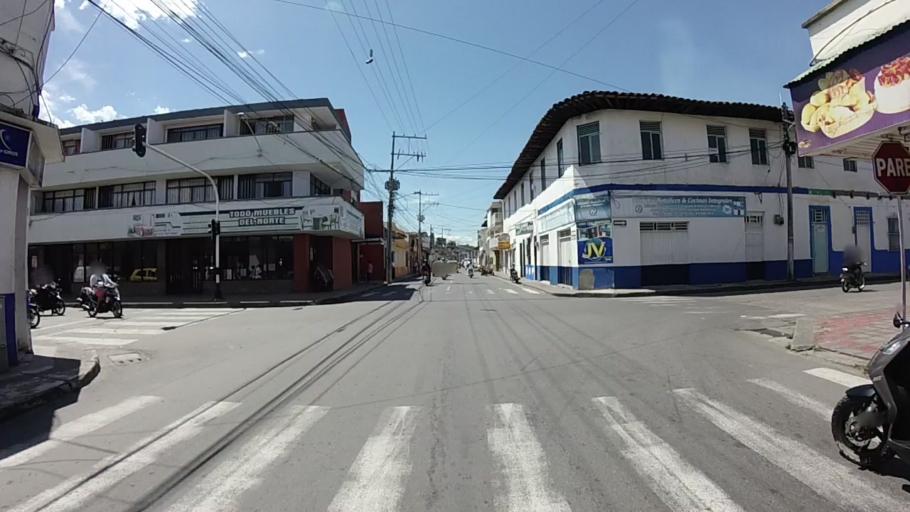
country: CO
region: Valle del Cauca
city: Cartago
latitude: 4.7472
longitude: -75.9104
